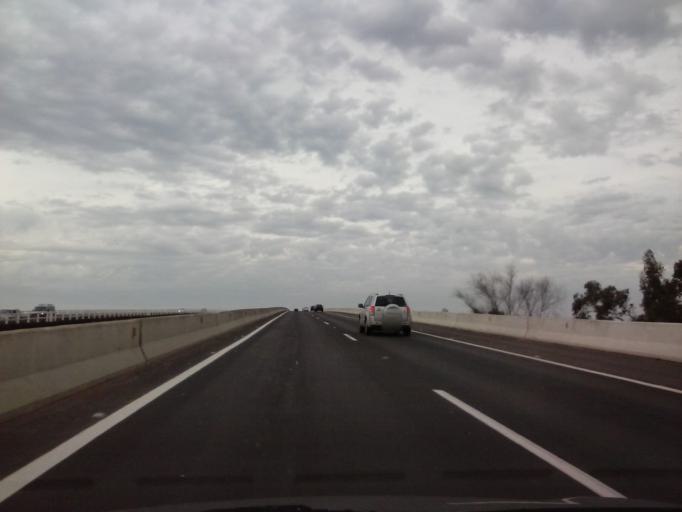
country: BR
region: Rio Grande do Sul
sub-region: Porto Alegre
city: Porto Alegre
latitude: -29.9928
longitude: -51.2746
